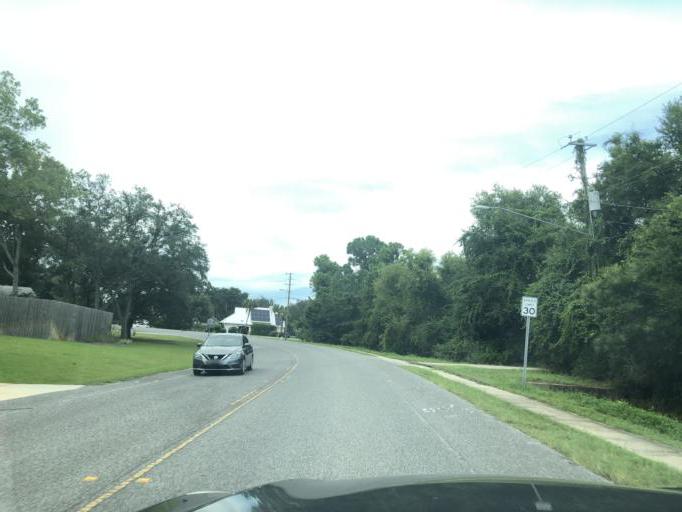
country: US
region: Florida
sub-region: Okaloosa County
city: Destin
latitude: 30.4074
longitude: -86.4952
